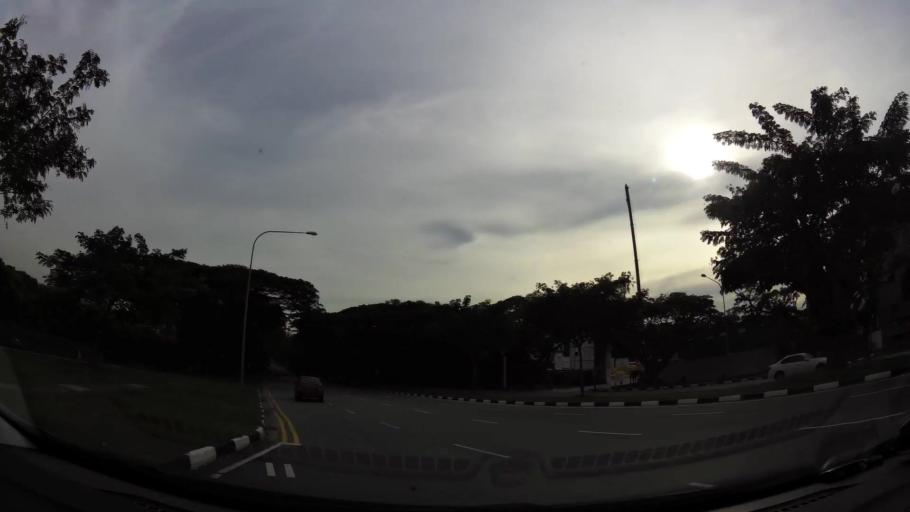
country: SG
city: Singapore
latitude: 1.3480
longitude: 103.8395
